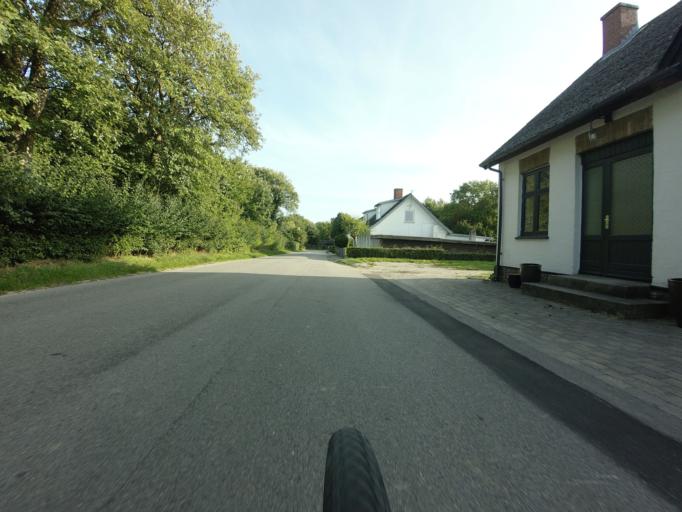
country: DK
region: Zealand
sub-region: Stevns Kommune
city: Store Heddinge
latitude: 55.2433
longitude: 12.3020
